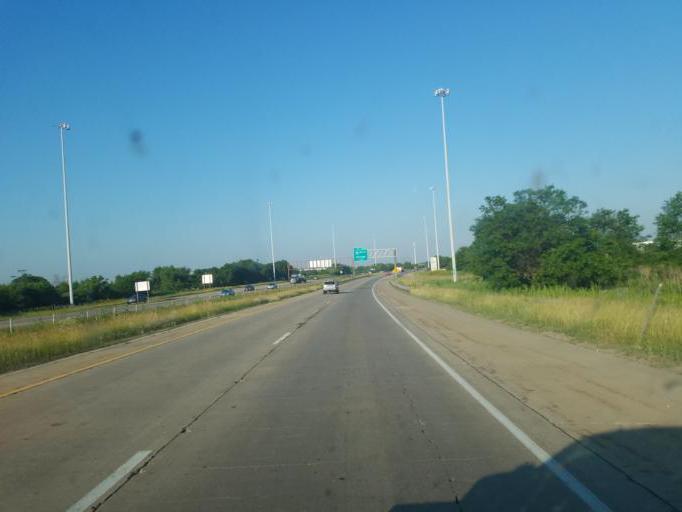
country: US
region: Illinois
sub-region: Will County
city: Shorewood
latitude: 41.4910
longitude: -88.1689
